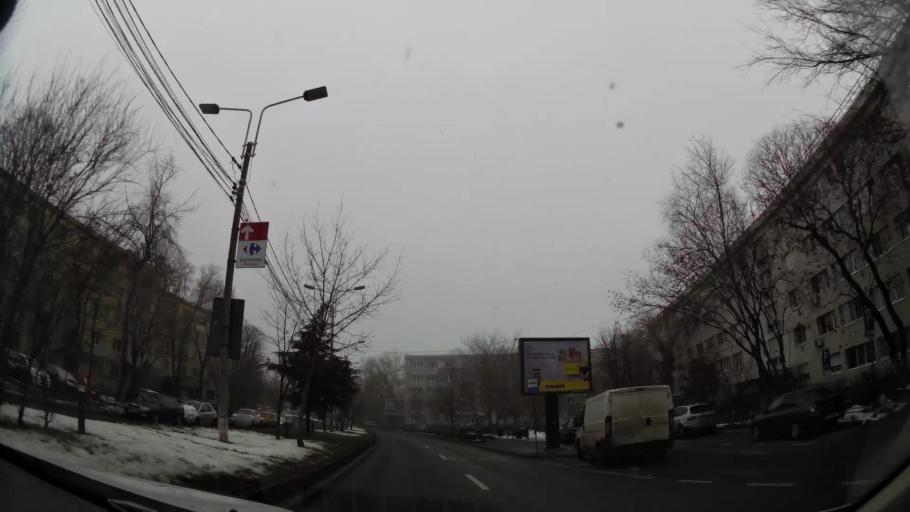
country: RO
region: Ilfov
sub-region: Comuna Chiajna
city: Rosu
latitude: 44.4595
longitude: 26.0402
